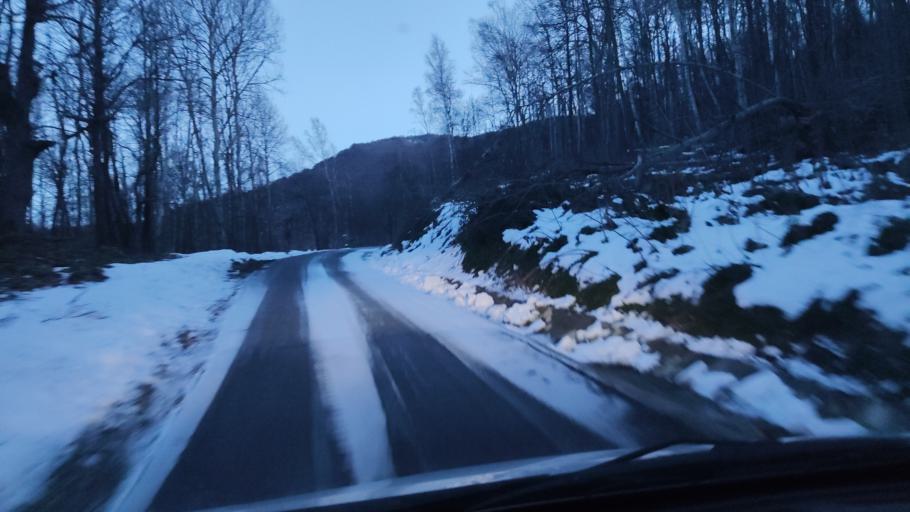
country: IT
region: Piedmont
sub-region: Provincia di Cuneo
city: Viola
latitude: 44.2755
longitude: 7.9672
